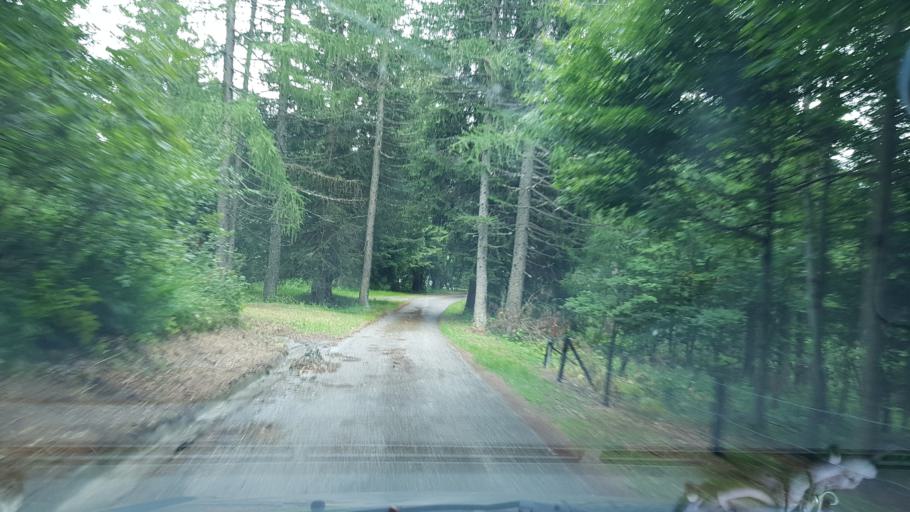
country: IT
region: Friuli Venezia Giulia
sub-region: Provincia di Udine
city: Cercivento
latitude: 46.5478
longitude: 12.9857
